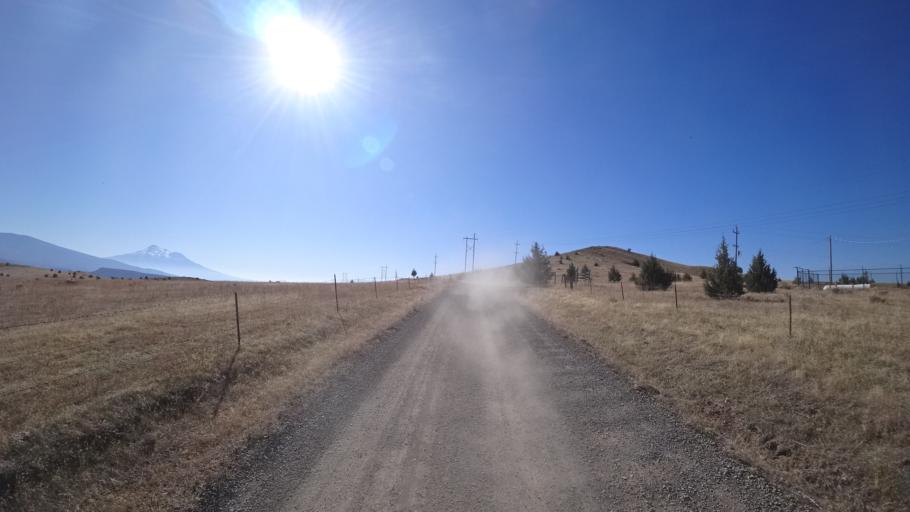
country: US
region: California
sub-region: Siskiyou County
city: Montague
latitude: 41.7755
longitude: -122.3581
